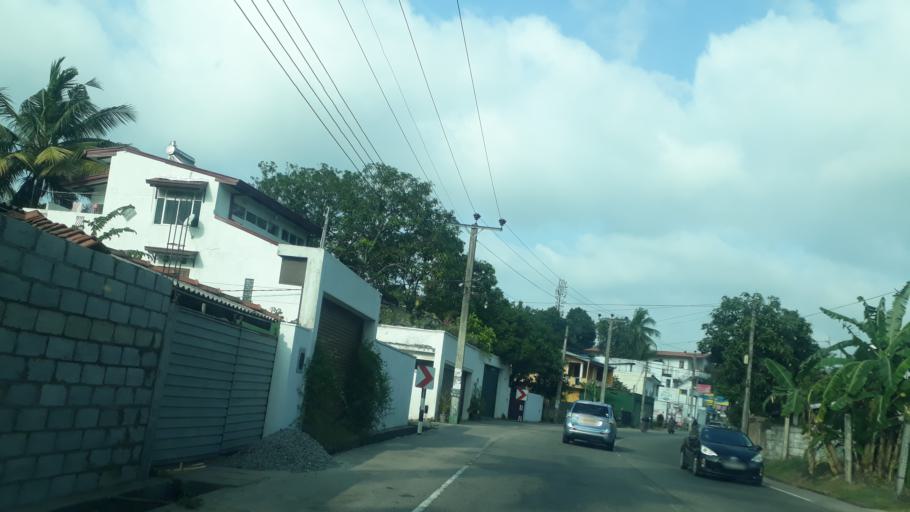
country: LK
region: Western
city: Battaramulla South
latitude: 6.8933
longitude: 79.9386
